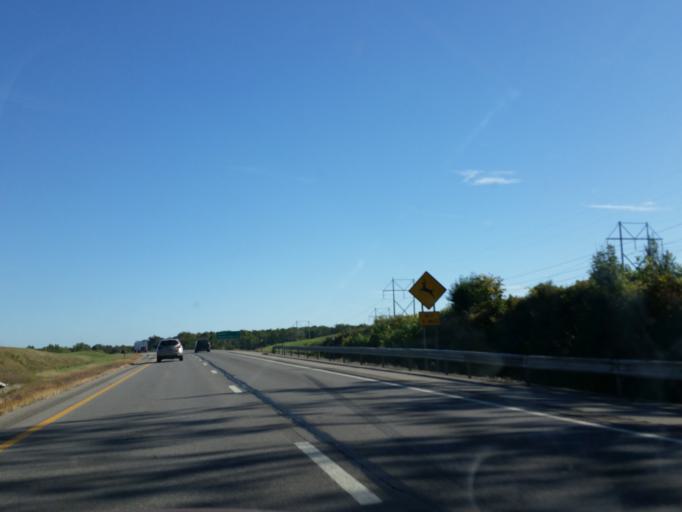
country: US
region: New York
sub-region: Erie County
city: Blasdell
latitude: 42.7618
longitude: -78.8220
